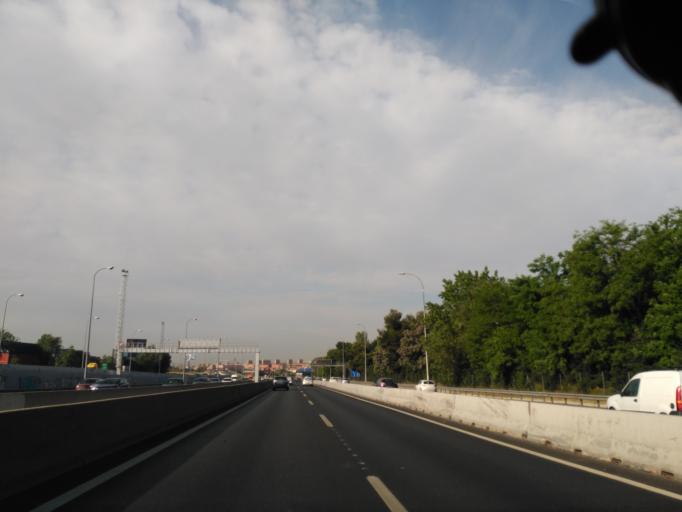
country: ES
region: Madrid
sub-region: Provincia de Madrid
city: Puente de Vallecas
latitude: 40.3892
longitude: -3.6798
